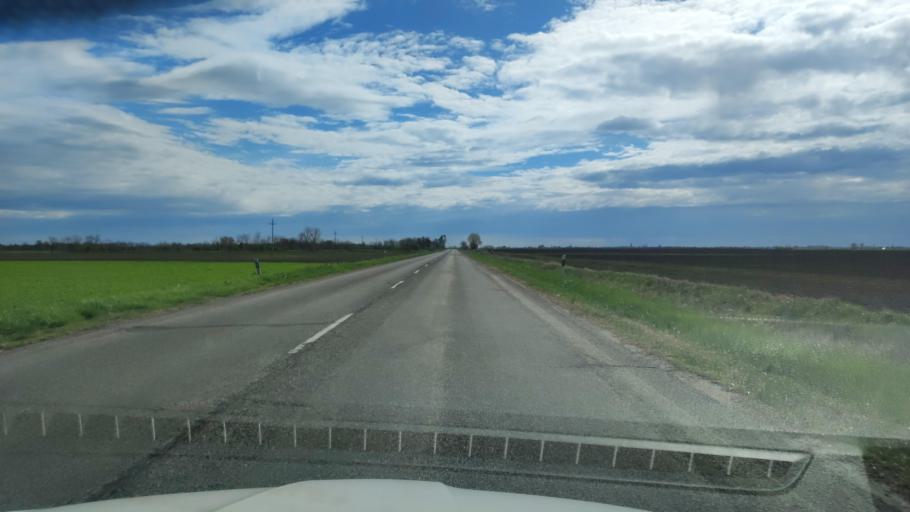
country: HU
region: Pest
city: Abony
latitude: 47.1877
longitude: 19.9493
